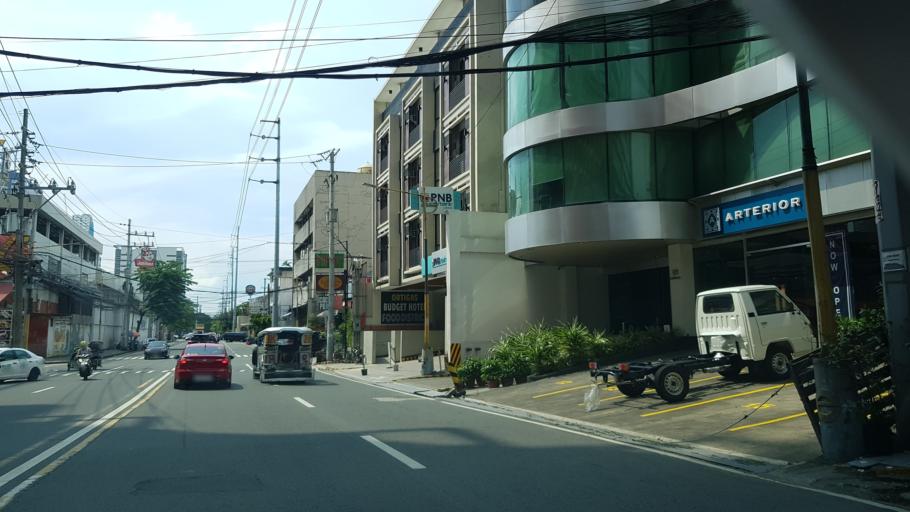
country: PH
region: Metro Manila
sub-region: Pasig
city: Pasig City
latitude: 14.5734
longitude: 121.0595
